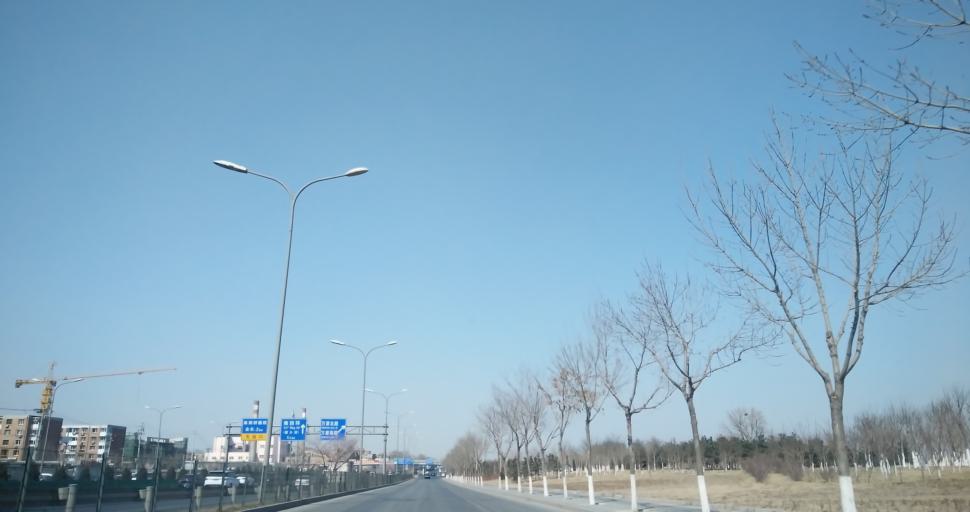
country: CN
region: Beijing
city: Jiugong
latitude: 39.7902
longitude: 116.4244
